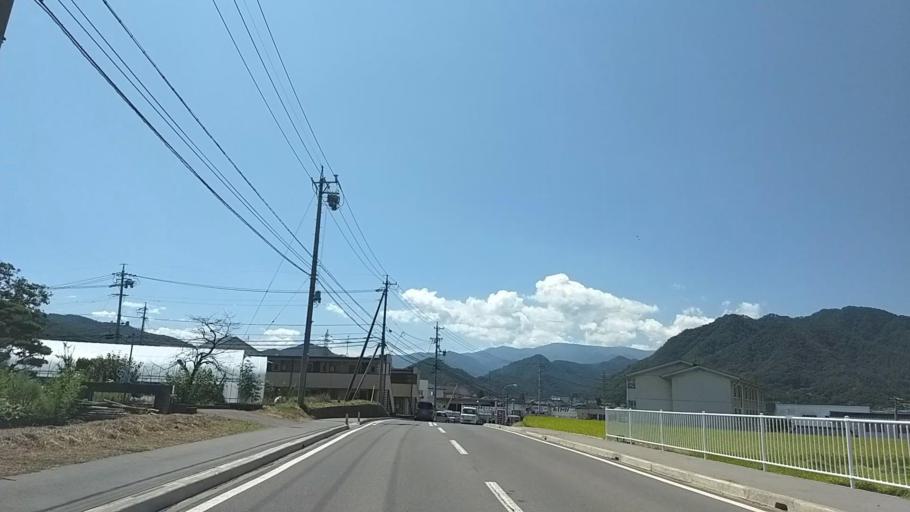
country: JP
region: Nagano
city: Kamimaruko
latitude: 36.3401
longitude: 138.2813
